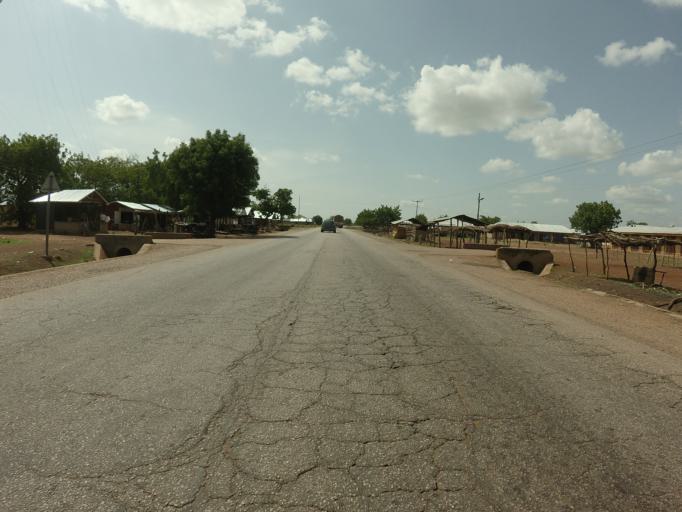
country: GH
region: Northern
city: Savelugu
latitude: 9.8724
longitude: -0.8720
